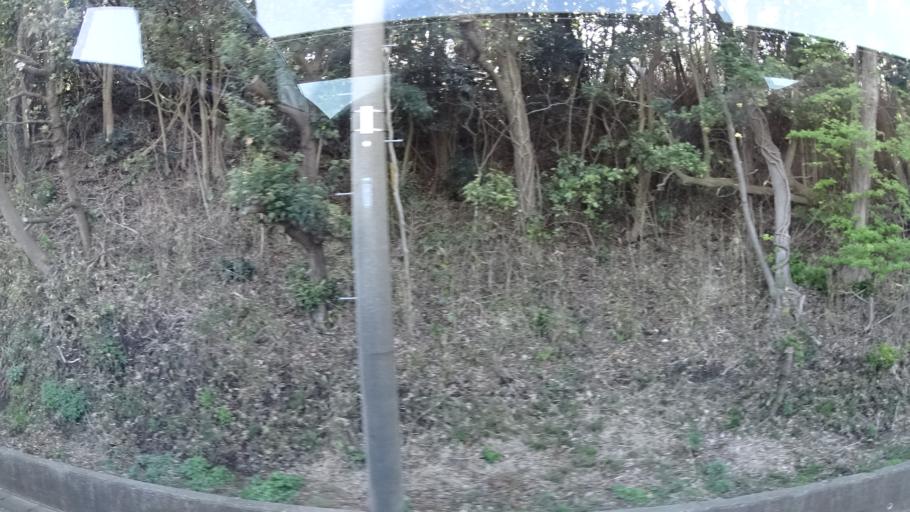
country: JP
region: Kanagawa
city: Miura
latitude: 35.1529
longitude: 139.6459
